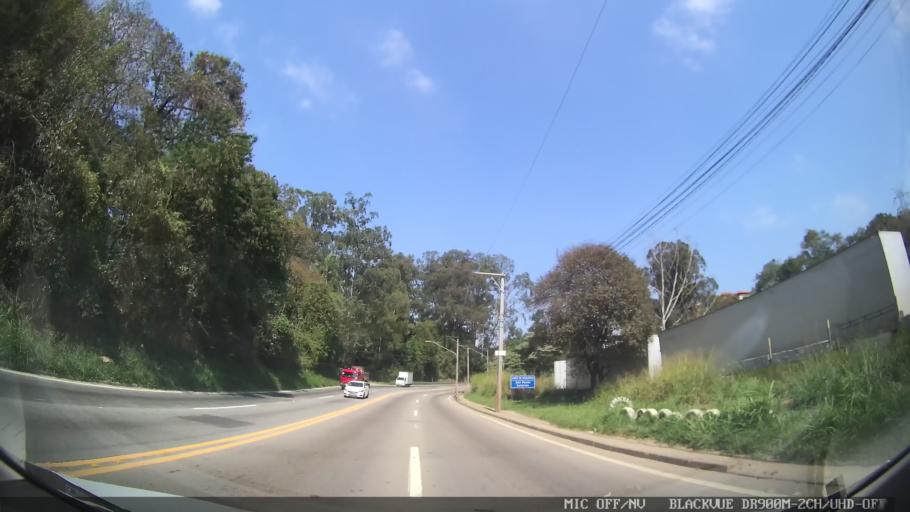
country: BR
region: Sao Paulo
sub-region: Caieiras
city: Caieiras
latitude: -23.4015
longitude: -46.7200
